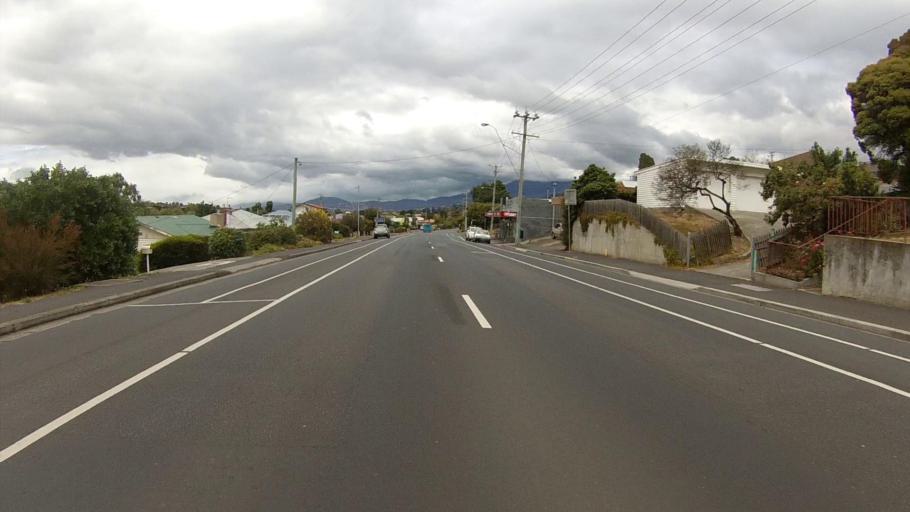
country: AU
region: Tasmania
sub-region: Glenorchy
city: Claremont
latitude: -42.7796
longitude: 147.2521
